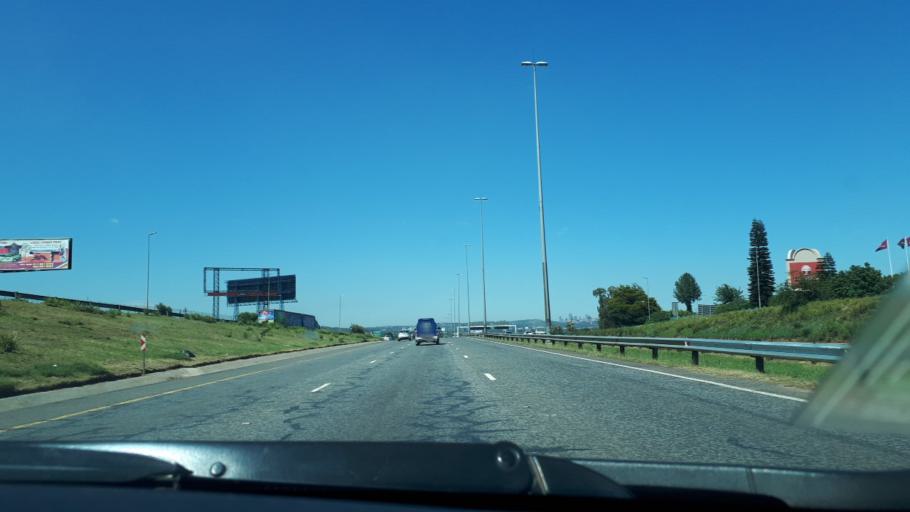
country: ZA
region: Gauteng
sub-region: City of Johannesburg Metropolitan Municipality
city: Modderfontein
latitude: -26.1383
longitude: 28.1950
